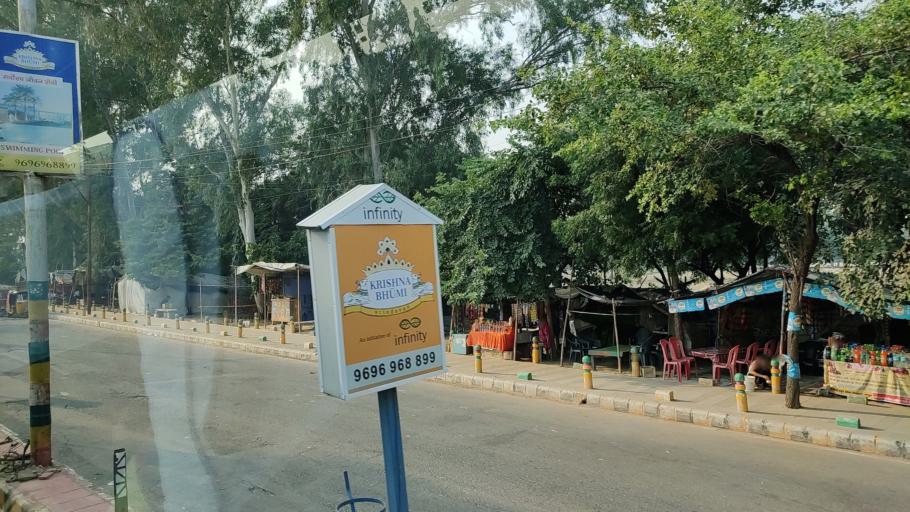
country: IN
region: Uttar Pradesh
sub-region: Mathura
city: Vrindavan
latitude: 27.5629
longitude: 77.6340
